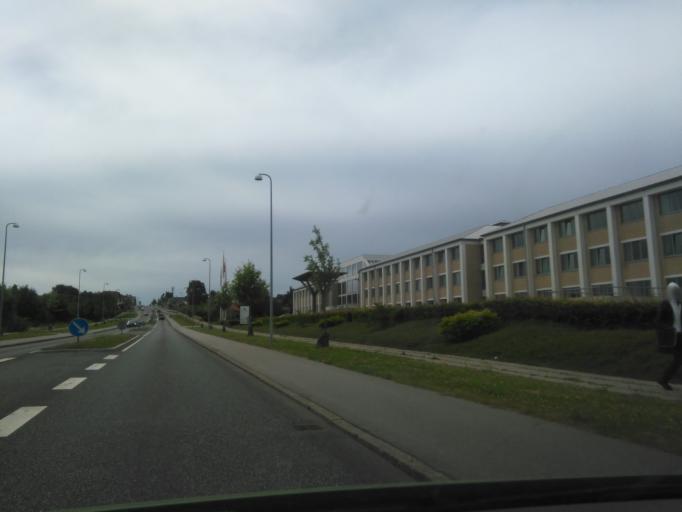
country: DK
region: Central Jutland
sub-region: Horsens Kommune
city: Horsens
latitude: 55.8782
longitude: 9.8433
